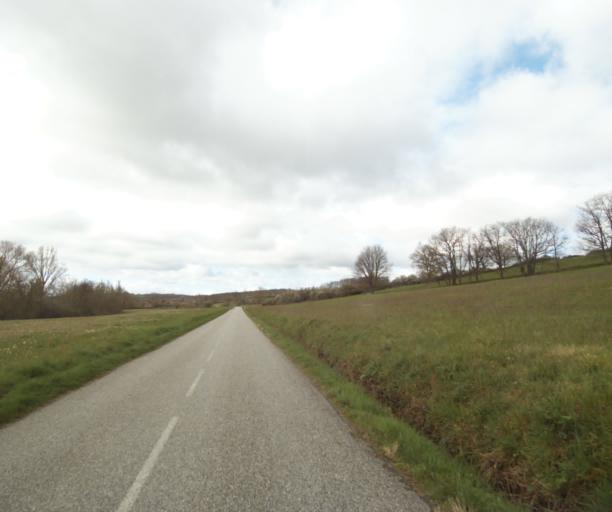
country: FR
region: Midi-Pyrenees
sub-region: Departement de l'Ariege
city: Saverdun
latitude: 43.2138
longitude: 1.5253
